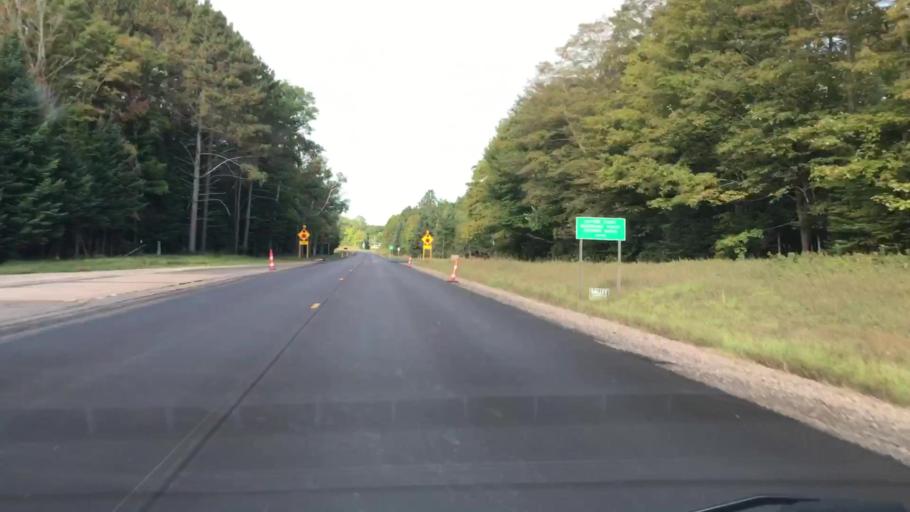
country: US
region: Michigan
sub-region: Luce County
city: Newberry
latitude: 46.3464
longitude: -85.0205
